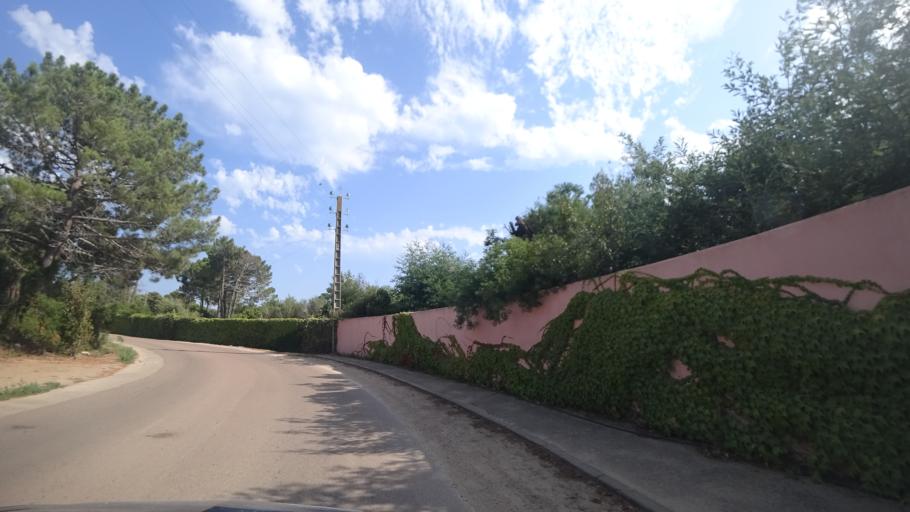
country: FR
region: Corsica
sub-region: Departement de la Corse-du-Sud
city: Porto-Vecchio
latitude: 41.6277
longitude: 9.3347
